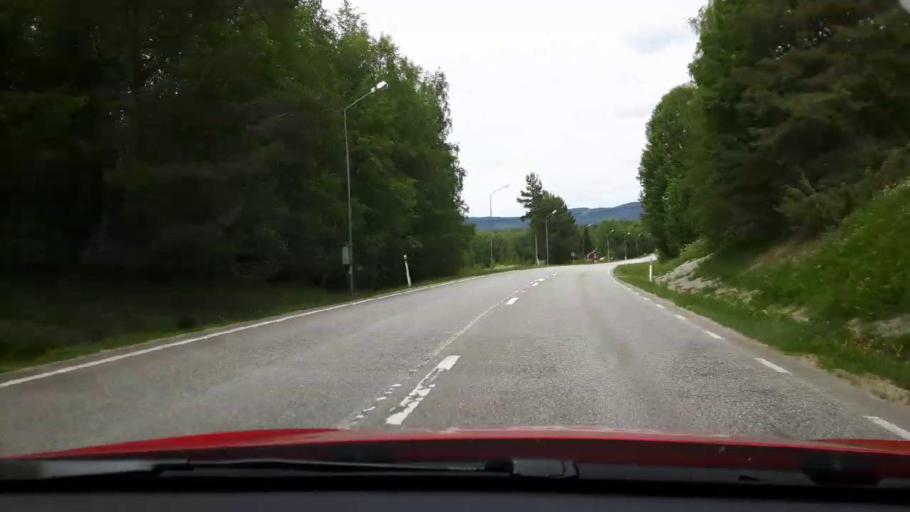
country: SE
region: Jaemtland
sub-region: Harjedalens Kommun
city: Sveg
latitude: 62.0660
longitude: 14.2736
